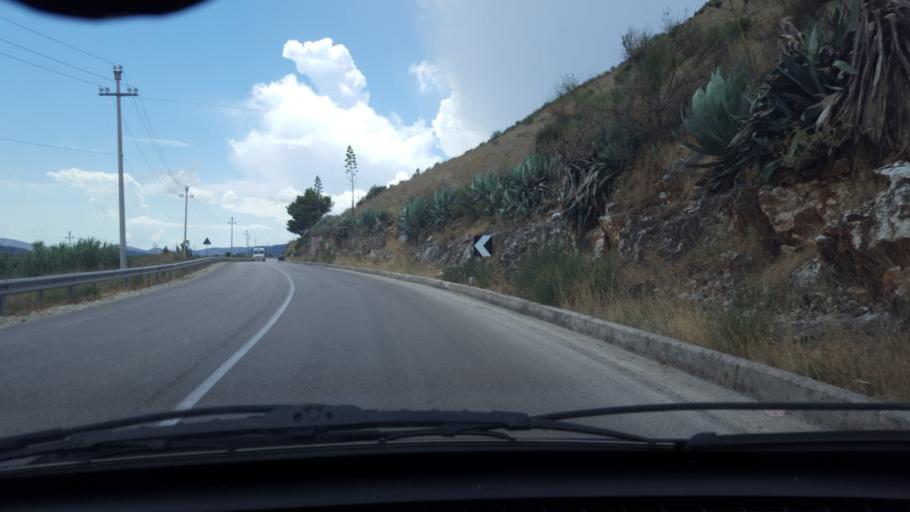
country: AL
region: Vlore
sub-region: Rrethi i Sarandes
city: Sarande
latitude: 39.8331
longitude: 20.0226
